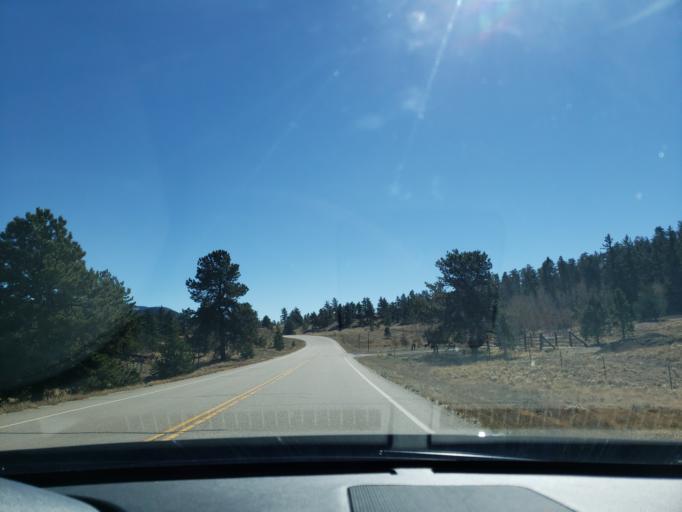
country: US
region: Colorado
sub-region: Chaffee County
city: Buena Vista
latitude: 38.8796
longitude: -105.6771
